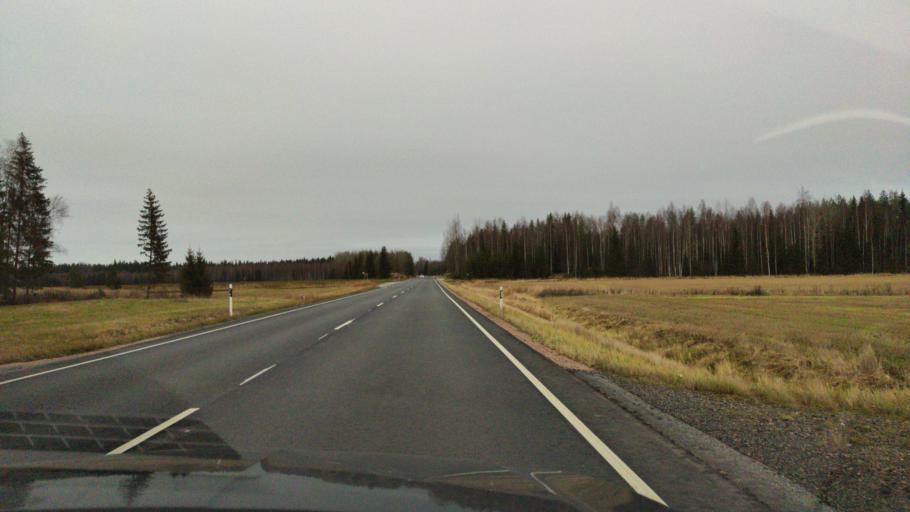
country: FI
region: Varsinais-Suomi
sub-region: Loimaa
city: Aura
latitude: 60.7108
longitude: 22.4434
